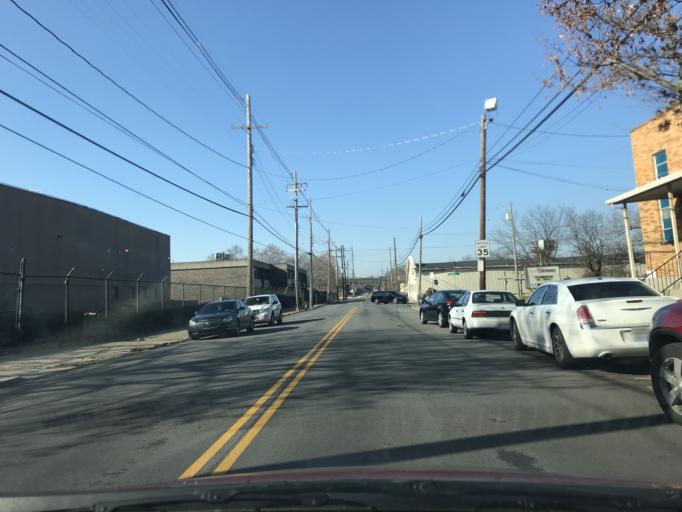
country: US
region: Kentucky
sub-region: Jefferson County
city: Louisville
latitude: 38.2259
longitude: -85.7481
